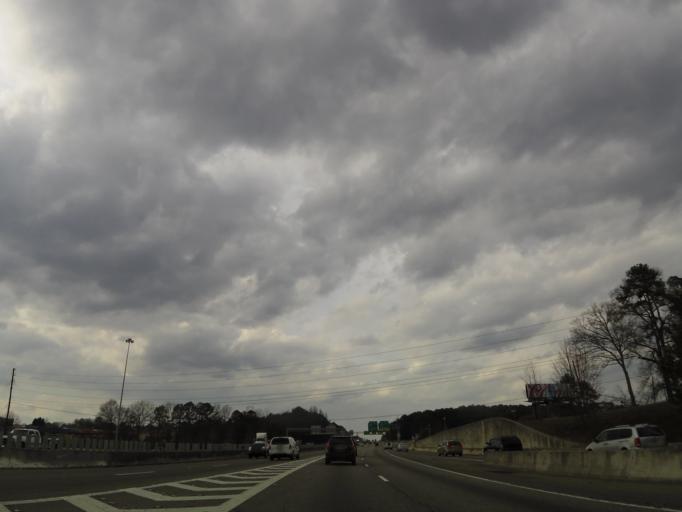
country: US
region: South Carolina
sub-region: Lexington County
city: Saint Andrews
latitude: 34.0308
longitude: -81.1040
